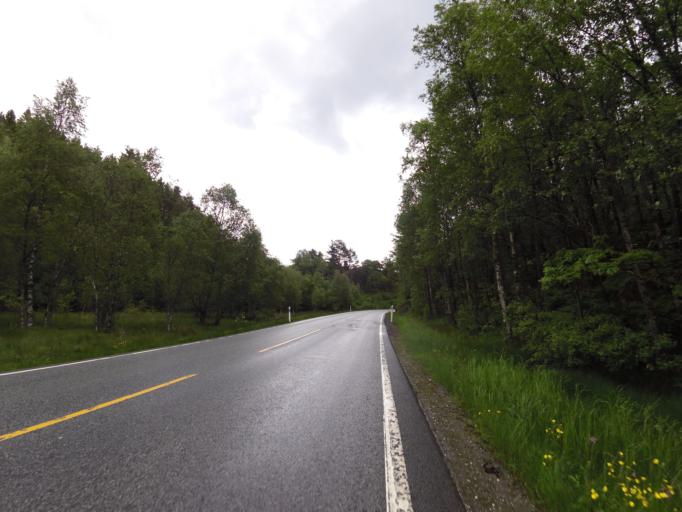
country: NO
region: Vest-Agder
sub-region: Farsund
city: Farsund
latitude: 58.1000
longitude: 6.8378
